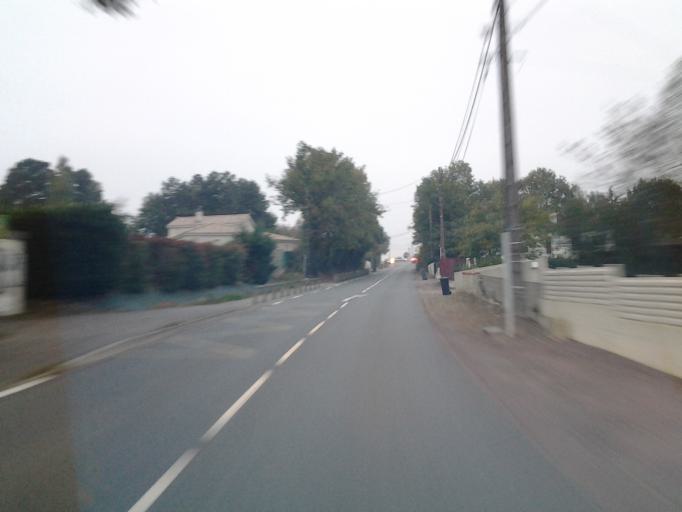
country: FR
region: Pays de la Loire
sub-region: Departement de la Vendee
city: La Roche-sur-Yon
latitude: 46.6480
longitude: -1.4122
